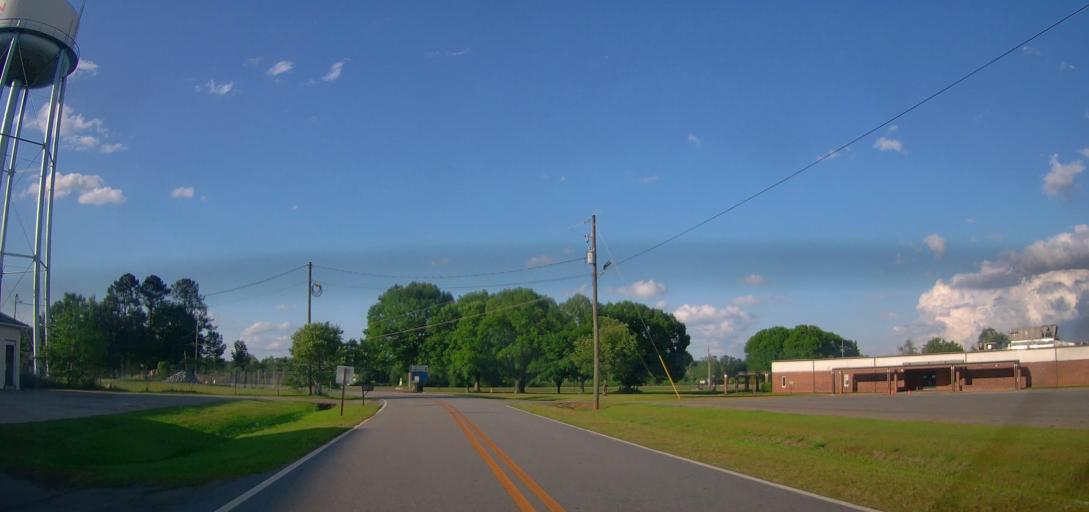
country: US
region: Georgia
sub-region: Peach County
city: Byron
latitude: 32.6505
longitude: -83.7536
